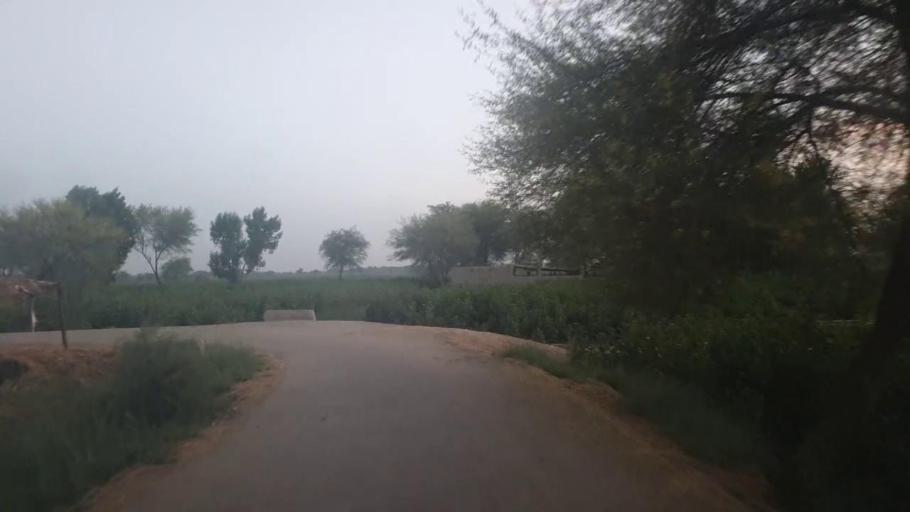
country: PK
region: Sindh
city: Ubauro
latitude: 28.1039
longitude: 69.7816
